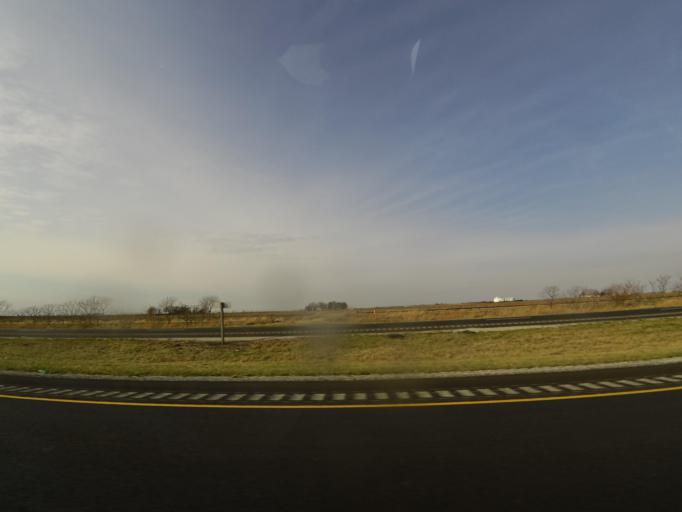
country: US
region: Illinois
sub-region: Macon County
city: Macon
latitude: 39.7398
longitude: -88.9899
